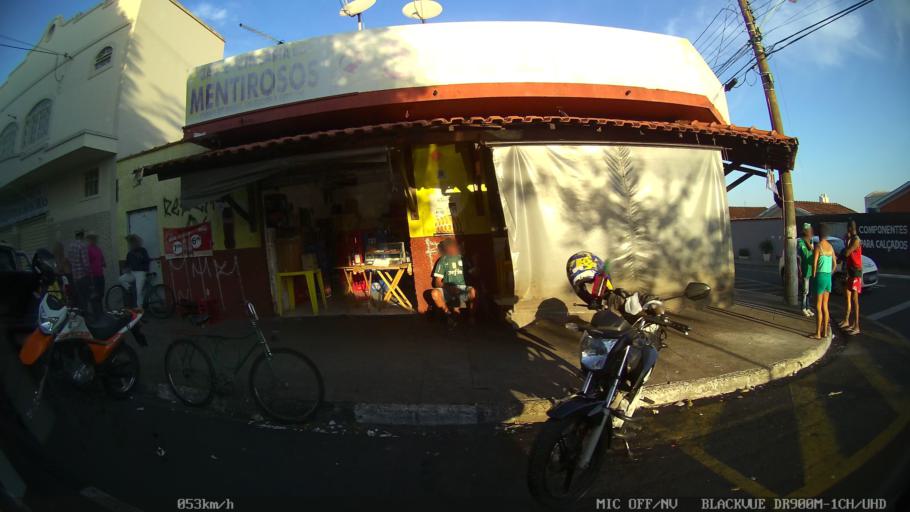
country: BR
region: Sao Paulo
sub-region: Franca
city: Franca
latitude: -20.5152
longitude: -47.3892
